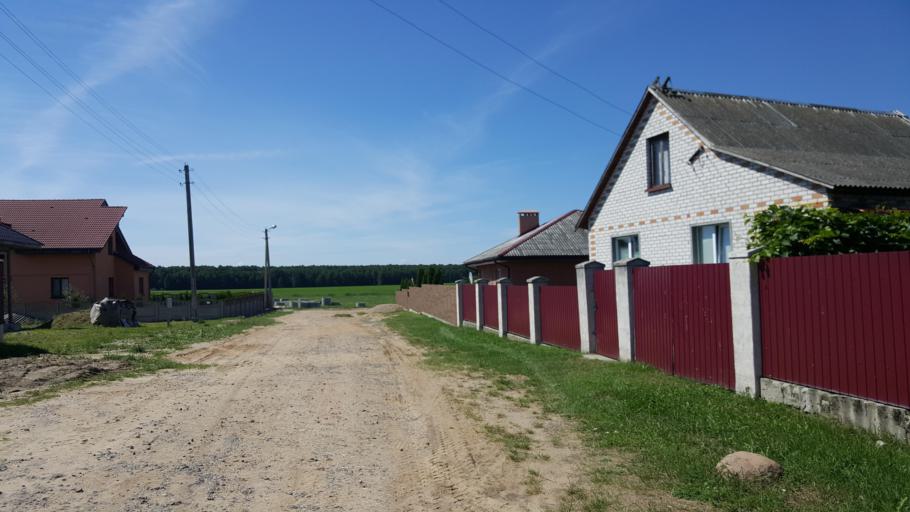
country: BY
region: Brest
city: Charnawchytsy
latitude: 52.2227
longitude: 23.7316
